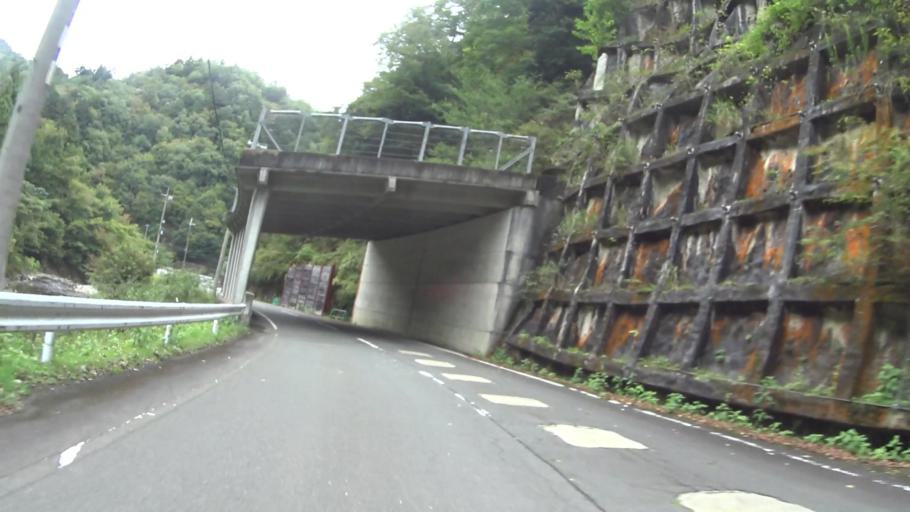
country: JP
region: Fukui
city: Obama
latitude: 35.3025
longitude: 135.6987
